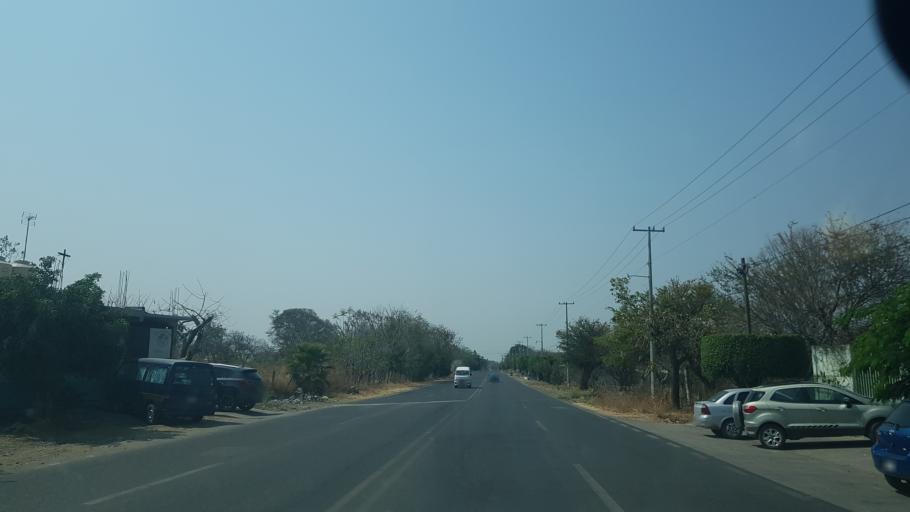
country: MX
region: Morelos
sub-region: Temoac
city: Temoac
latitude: 18.7643
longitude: -98.7792
